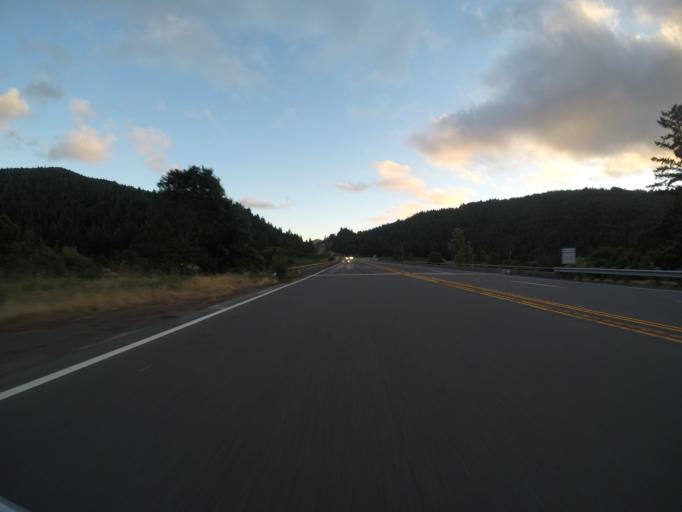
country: US
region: California
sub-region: Humboldt County
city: Redway
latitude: 40.0005
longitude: -123.7844
